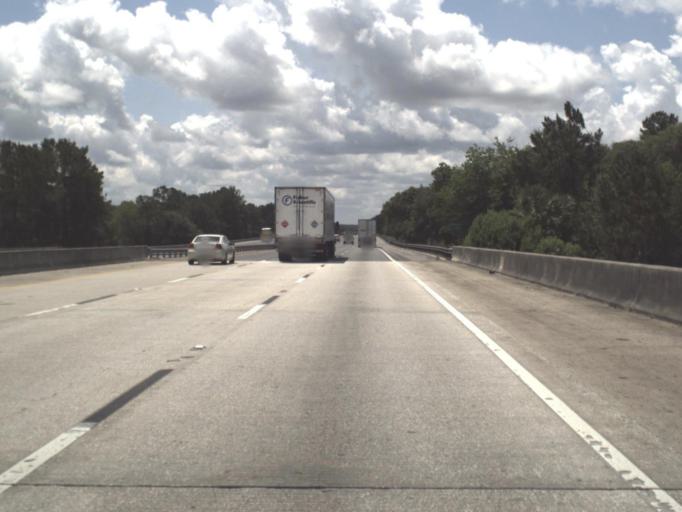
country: US
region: Florida
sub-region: Suwannee County
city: Wellborn
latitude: 30.3463
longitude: -82.8329
